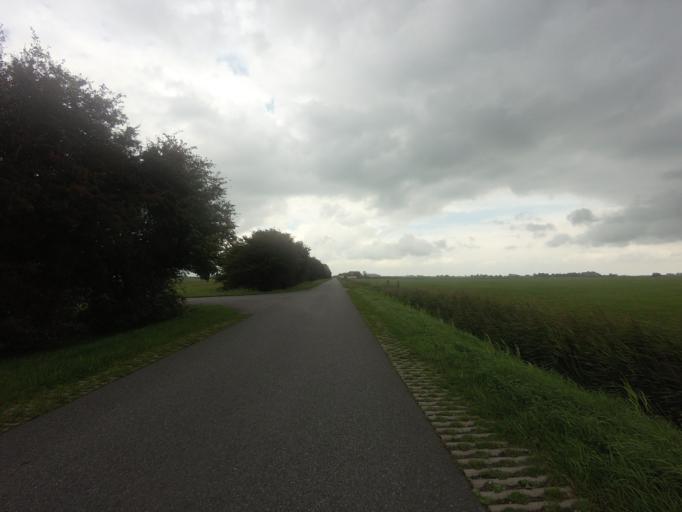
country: NL
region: Friesland
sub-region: Sudwest Fryslan
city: Makkum
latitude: 53.0201
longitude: 5.4201
